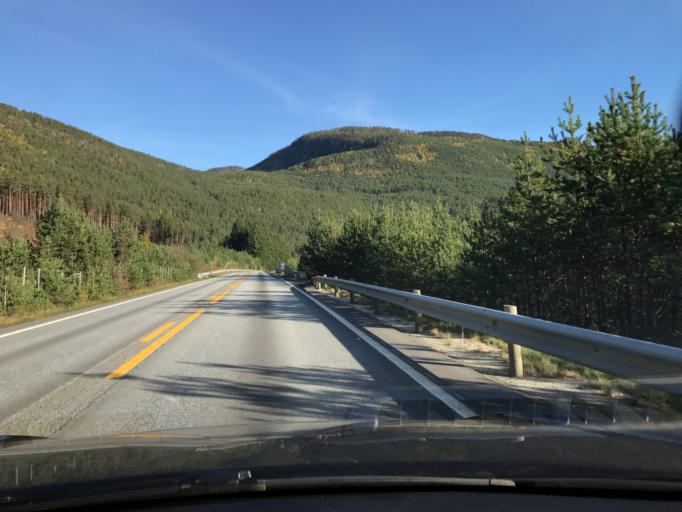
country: NO
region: Sogn og Fjordane
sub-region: Sogndal
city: Sogndalsfjora
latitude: 61.1815
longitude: 7.2876
